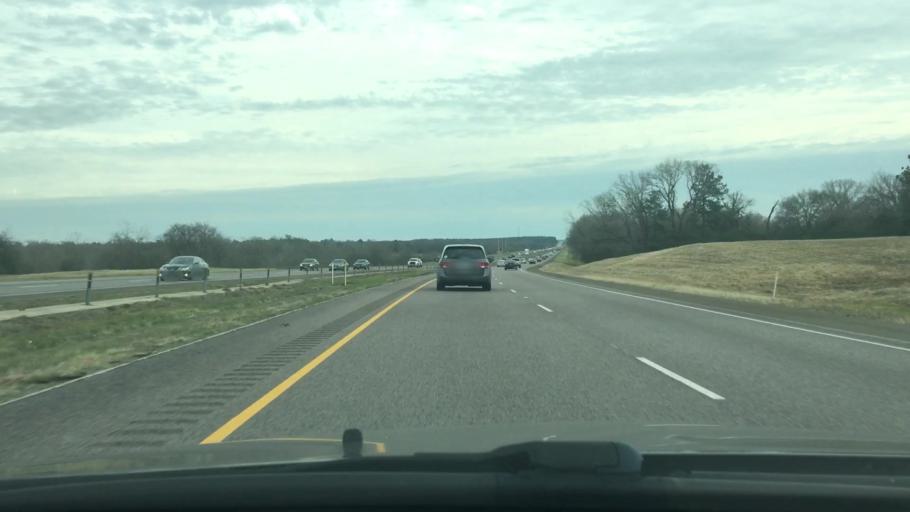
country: US
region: Texas
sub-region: Madison County
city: Madisonville
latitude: 30.9080
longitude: -95.7885
